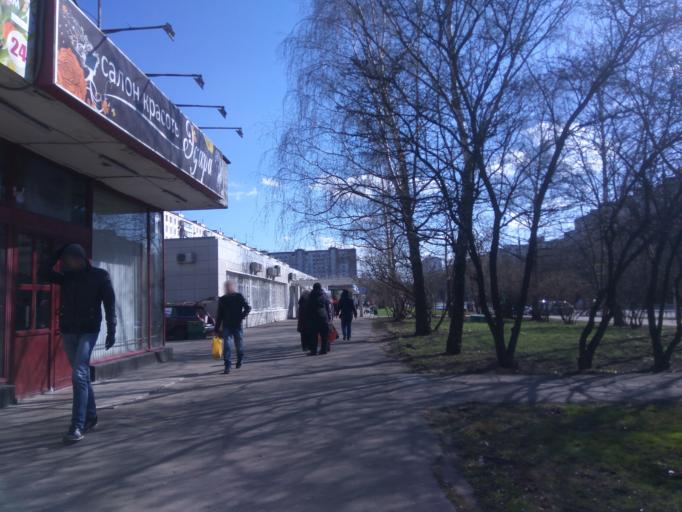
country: RU
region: Moscow
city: Ivanovskoye
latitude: 55.7648
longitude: 37.8330
